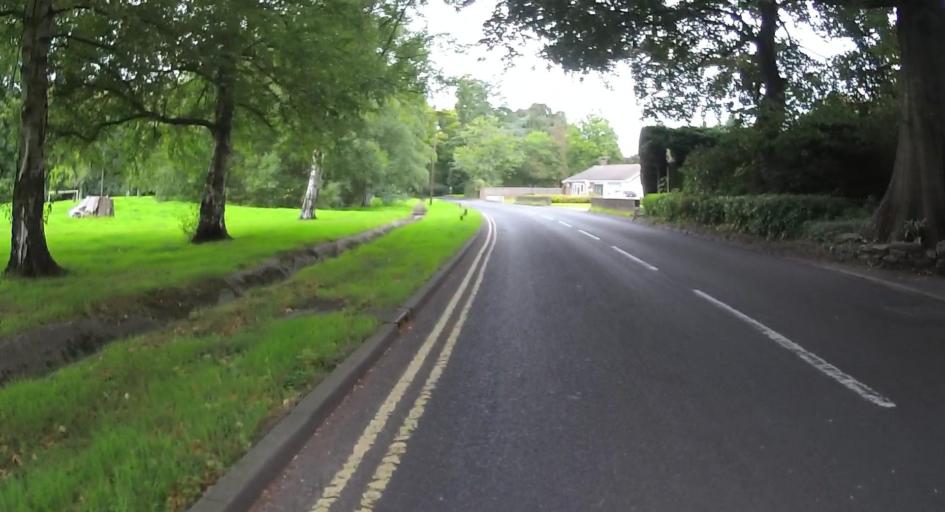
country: GB
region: England
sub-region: Surrey
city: Knaphill
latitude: 51.3232
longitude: -0.6097
